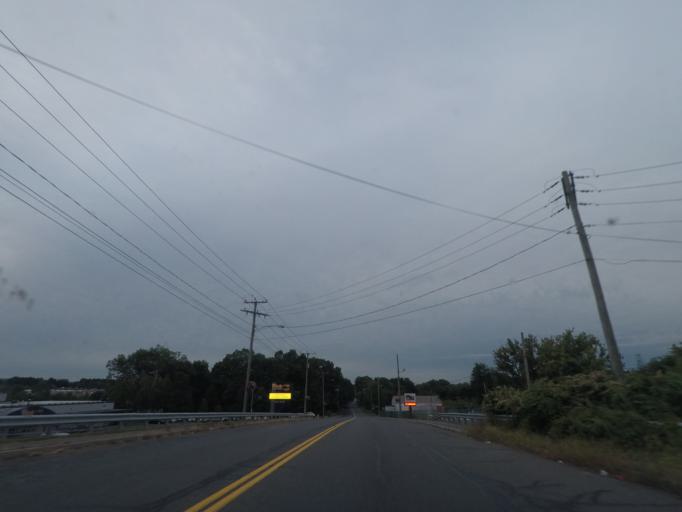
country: US
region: Massachusetts
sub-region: Hampden County
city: Ludlow
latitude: 42.1451
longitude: -72.5032
